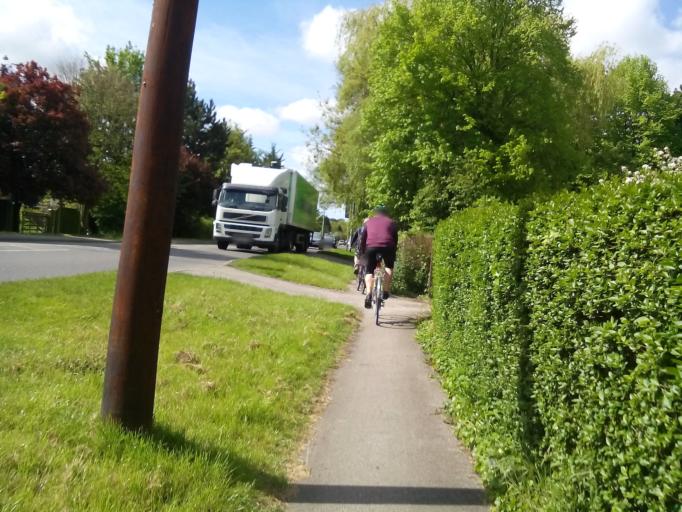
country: GB
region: England
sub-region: Cambridgeshire
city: Harston
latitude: 52.1451
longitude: 0.0891
